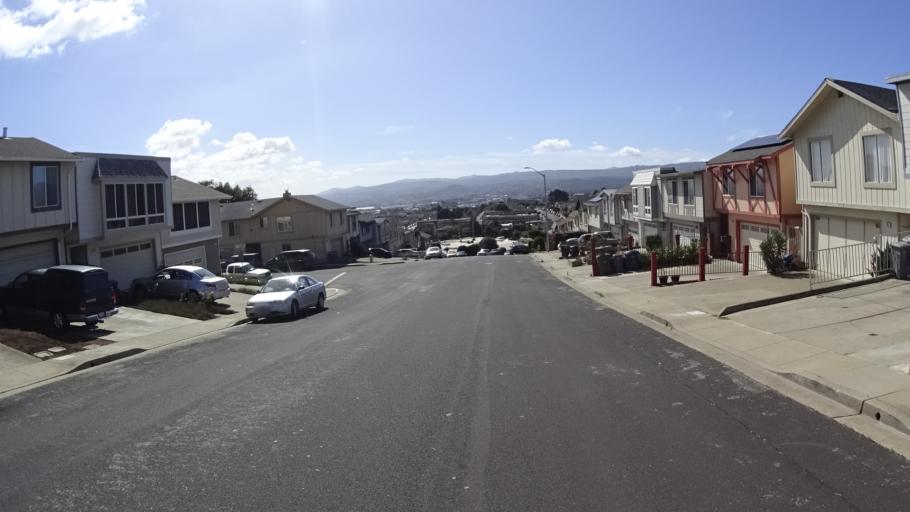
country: US
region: California
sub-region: San Mateo County
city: South San Francisco
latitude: 37.6651
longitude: -122.4074
